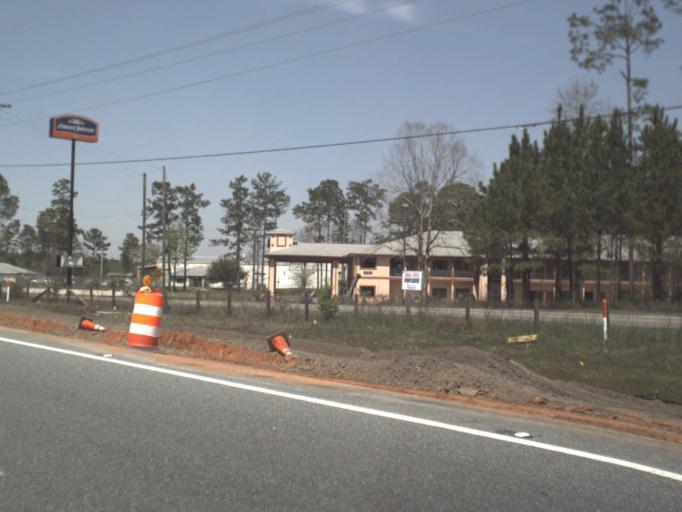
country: US
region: Florida
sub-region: Gadsden County
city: Midway
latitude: 30.4923
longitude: -84.4270
